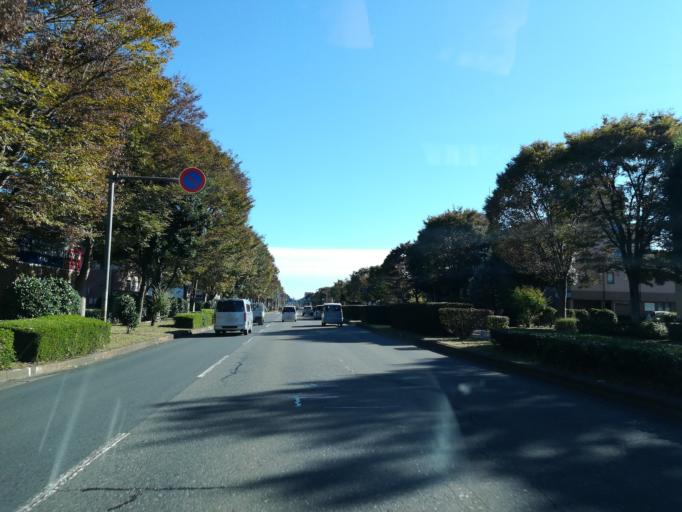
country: JP
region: Ibaraki
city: Naka
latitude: 36.0762
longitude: 140.1110
